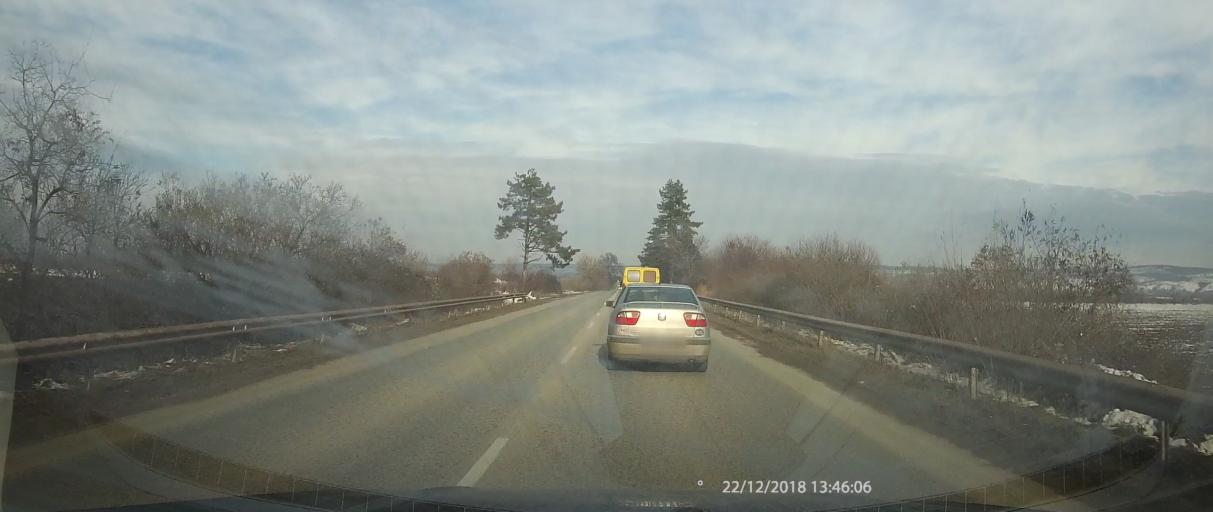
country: BG
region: Lovech
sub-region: Obshtina Lukovit
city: Lukovit
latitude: 43.2191
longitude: 24.1674
